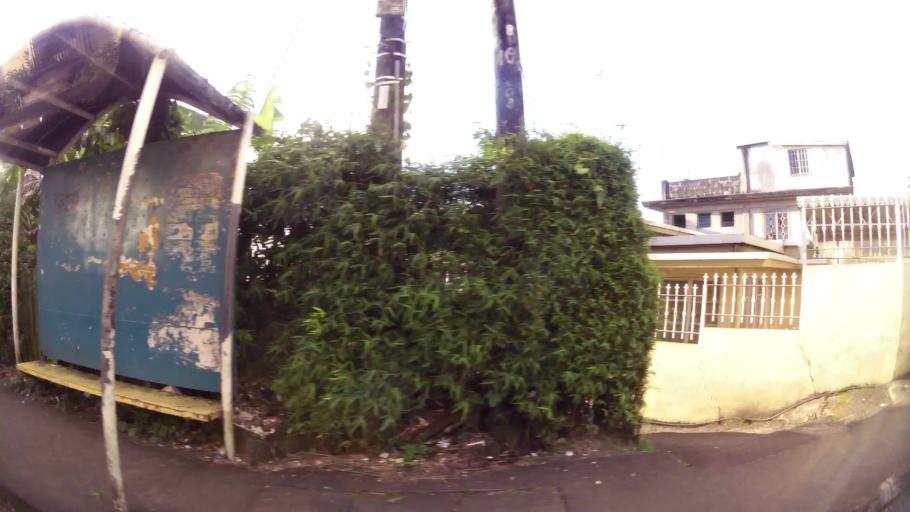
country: MU
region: Plaines Wilhems
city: Curepipe
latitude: -20.3050
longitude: 57.5316
